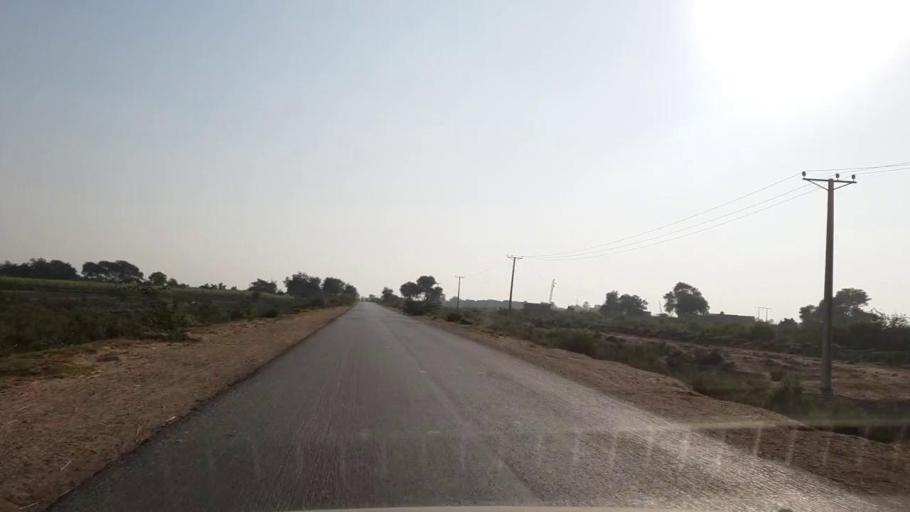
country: PK
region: Sindh
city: Bulri
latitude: 24.8914
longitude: 68.3440
